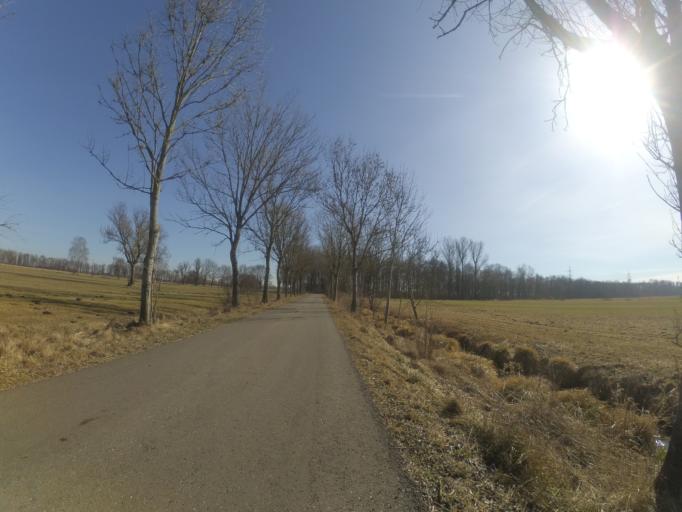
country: DE
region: Baden-Wuerttemberg
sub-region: Tuebingen Region
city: Rammingen
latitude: 48.4943
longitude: 10.1752
